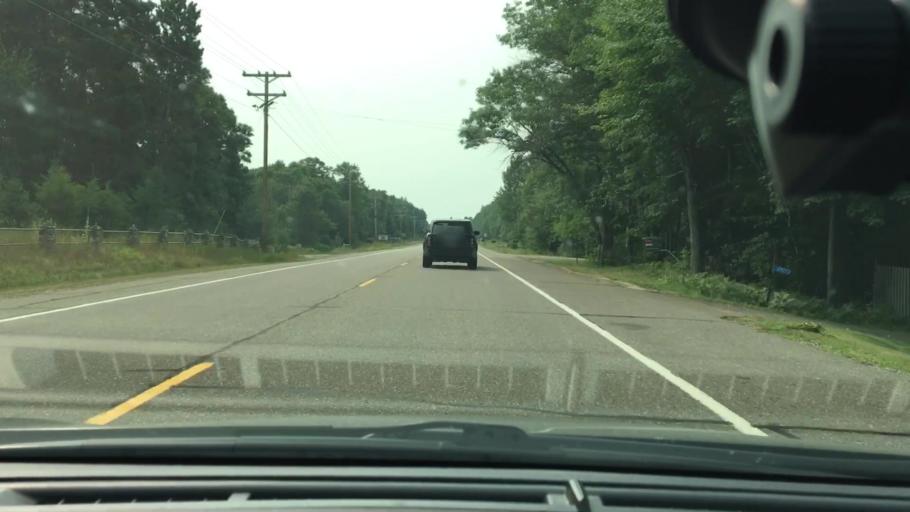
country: US
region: Minnesota
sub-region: Crow Wing County
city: Cross Lake
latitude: 46.5849
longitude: -94.1315
